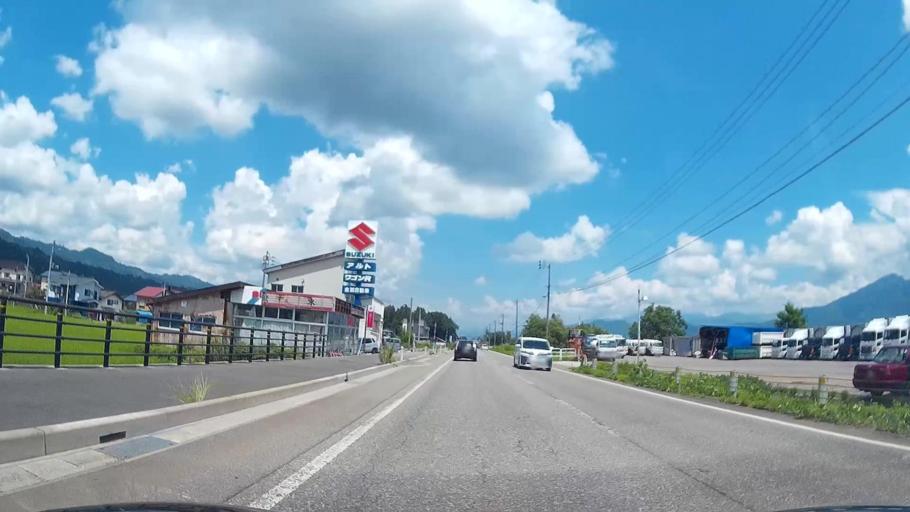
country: JP
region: Niigata
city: Shiozawa
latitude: 37.0096
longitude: 138.8226
